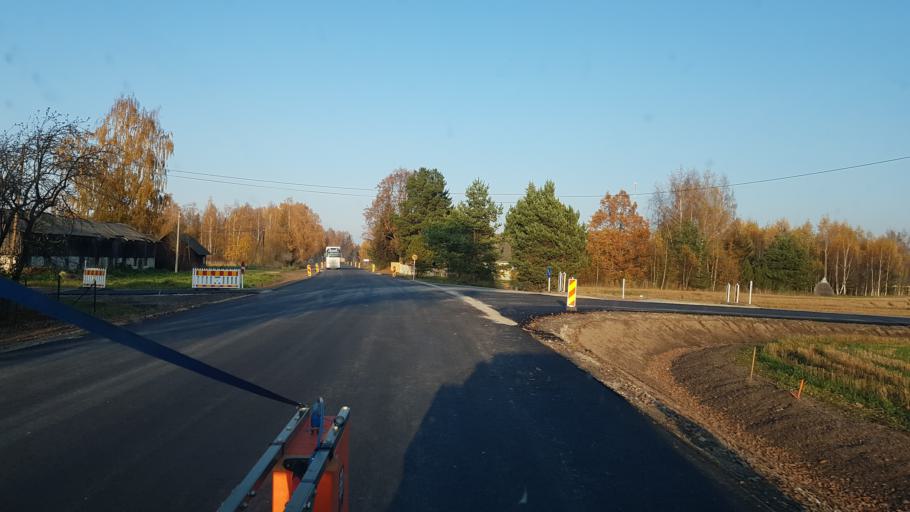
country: EE
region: Polvamaa
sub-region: Polva linn
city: Polva
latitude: 57.9438
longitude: 27.2119
